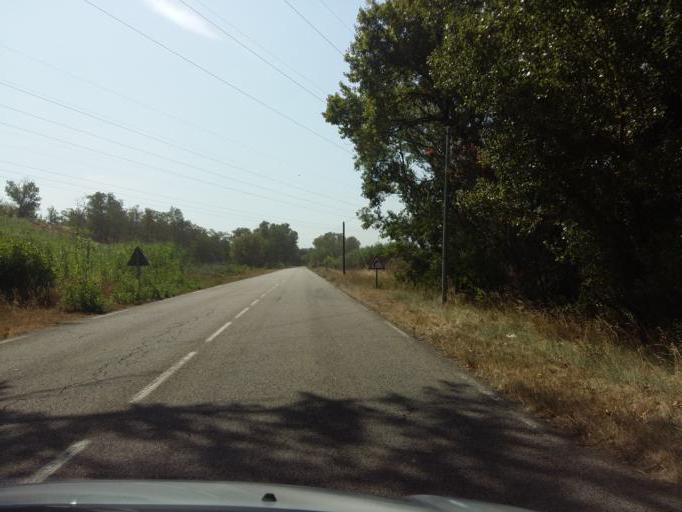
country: FR
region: Provence-Alpes-Cote d'Azur
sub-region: Departement du Vaucluse
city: Bollene
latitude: 44.3073
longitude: 4.7364
